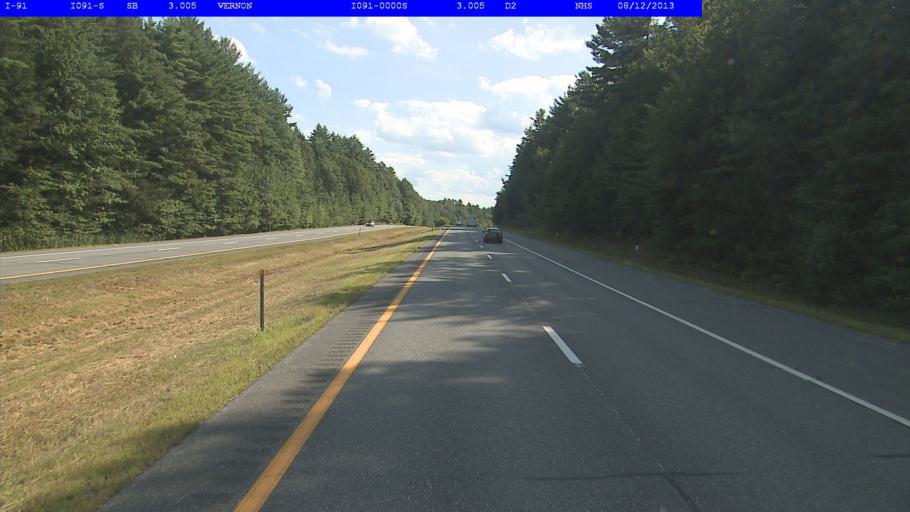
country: US
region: New Hampshire
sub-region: Cheshire County
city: Hinsdale
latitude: 42.7730
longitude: -72.5616
